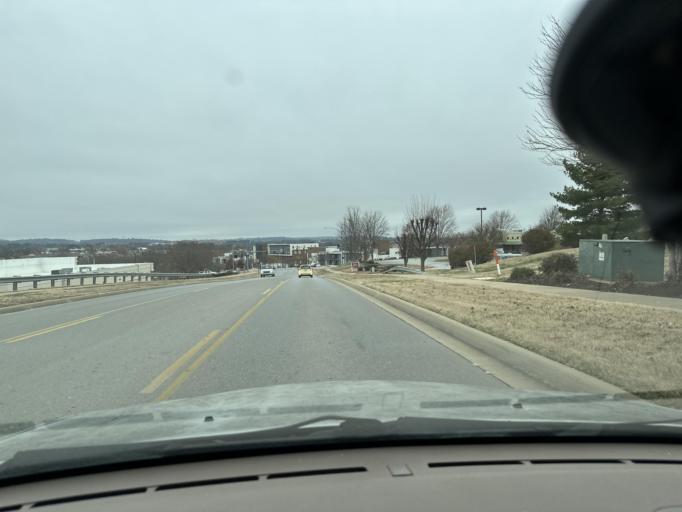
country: US
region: Arkansas
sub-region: Washington County
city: Johnson
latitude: 36.1262
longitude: -94.1556
